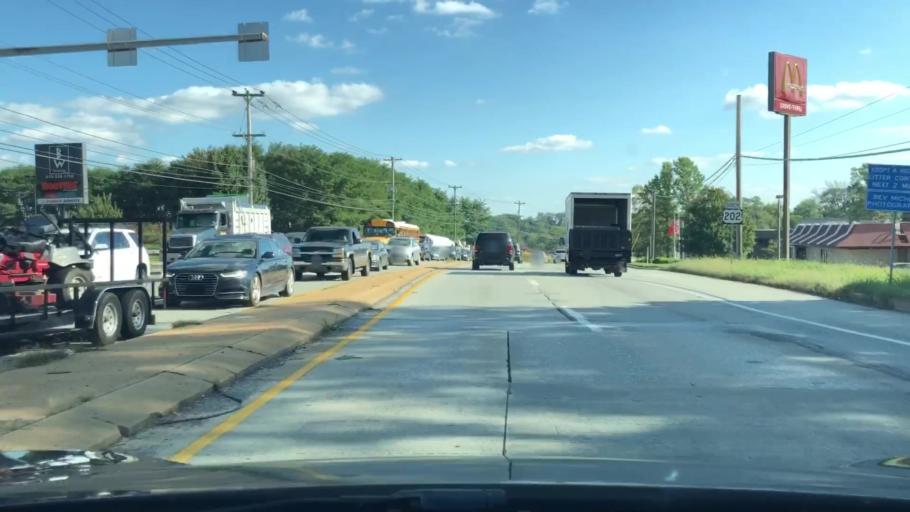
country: US
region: Pennsylvania
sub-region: Delaware County
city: Chester Heights
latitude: 39.8800
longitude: -75.5461
